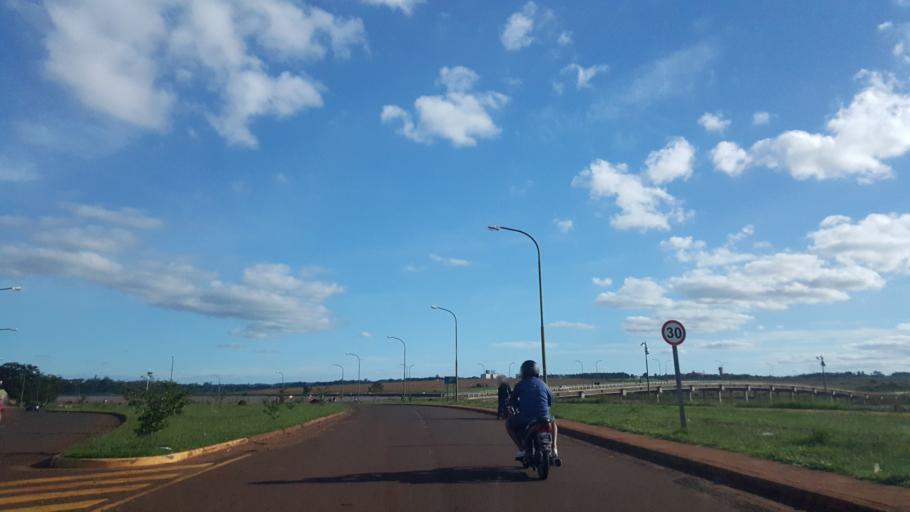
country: AR
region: Misiones
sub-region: Departamento de Capital
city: Posadas
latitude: -27.3802
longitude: -55.9524
